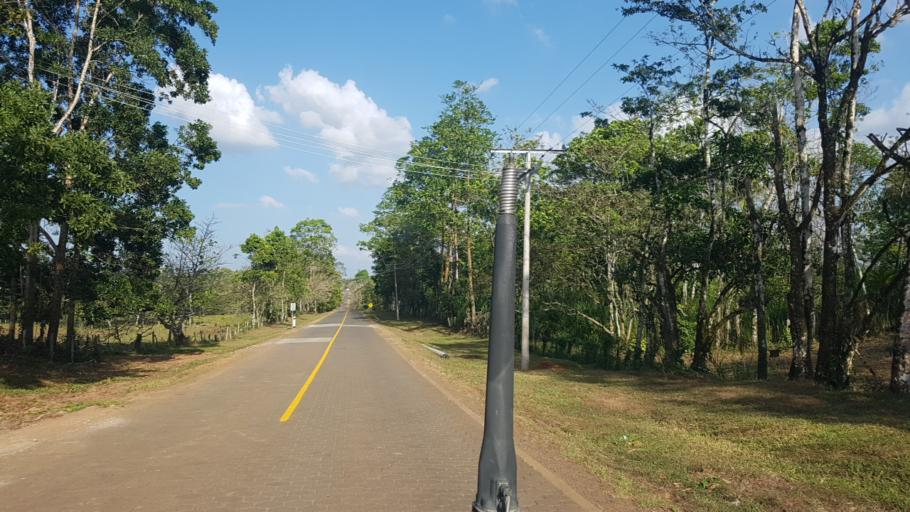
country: NI
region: Atlantico Sur
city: Nueva Guinea
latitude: 11.6900
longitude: -84.4239
